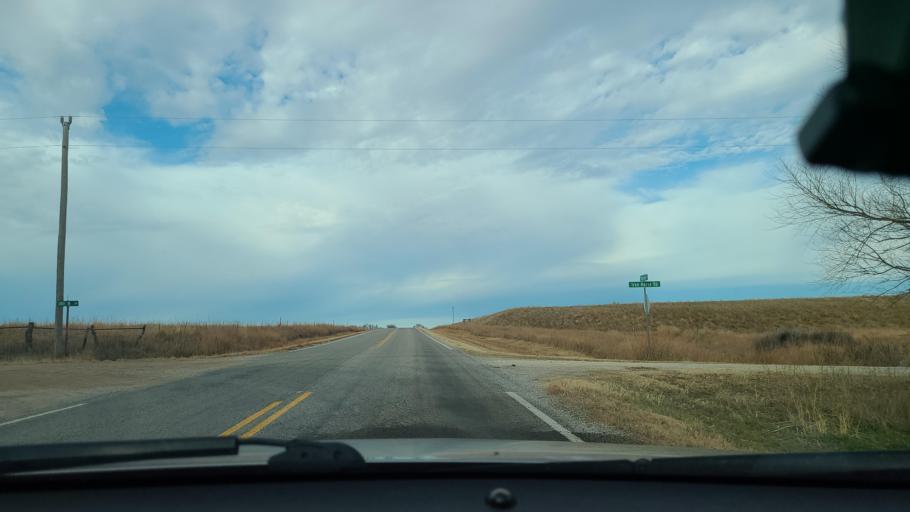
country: US
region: Kansas
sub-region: McPherson County
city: Inman
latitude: 38.3477
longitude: -97.9244
